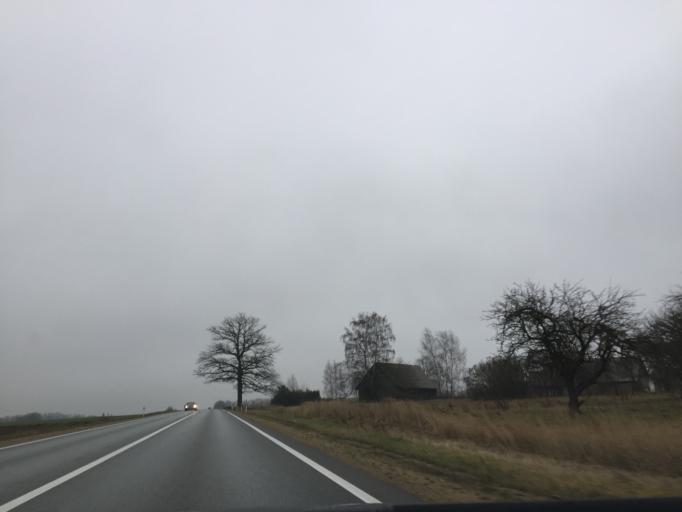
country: LV
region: Sigulda
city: Sigulda
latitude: 57.2562
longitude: 24.8630
